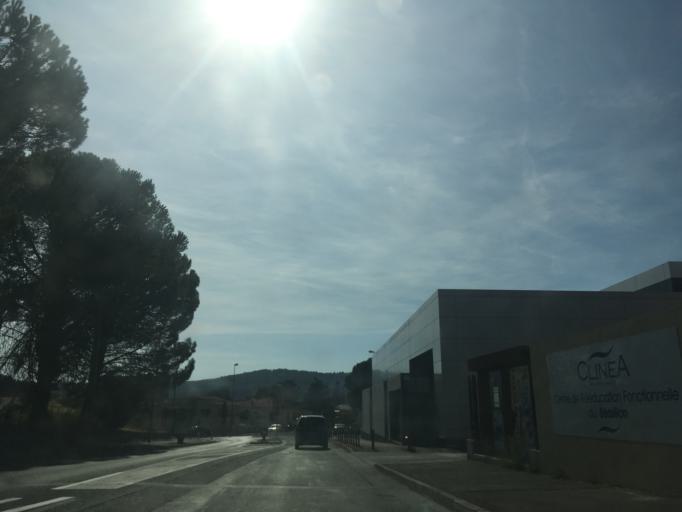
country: FR
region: Provence-Alpes-Cote d'Azur
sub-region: Departement du Var
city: Draguignan
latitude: 43.5321
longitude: 6.4746
